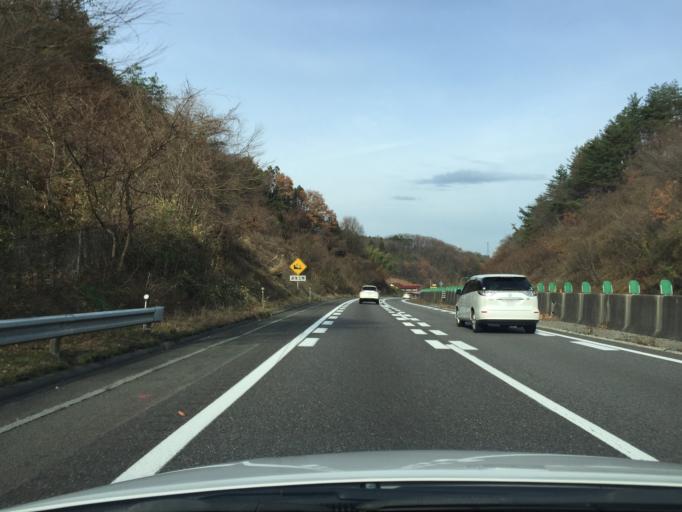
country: JP
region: Fukushima
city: Nihommatsu
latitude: 37.6269
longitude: 140.4317
